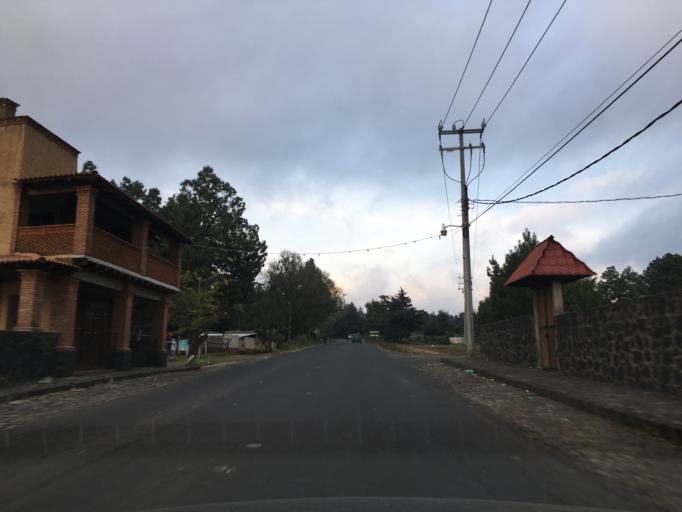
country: MX
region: Michoacan
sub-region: Uruapan
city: Santa Ana Zirosto
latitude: 19.5657
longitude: -102.2845
